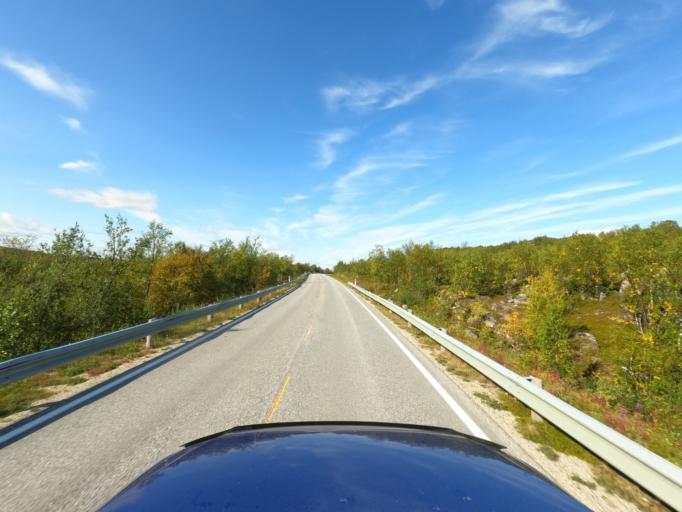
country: NO
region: Finnmark Fylke
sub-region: Porsanger
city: Lakselv
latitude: 69.7668
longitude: 25.1746
